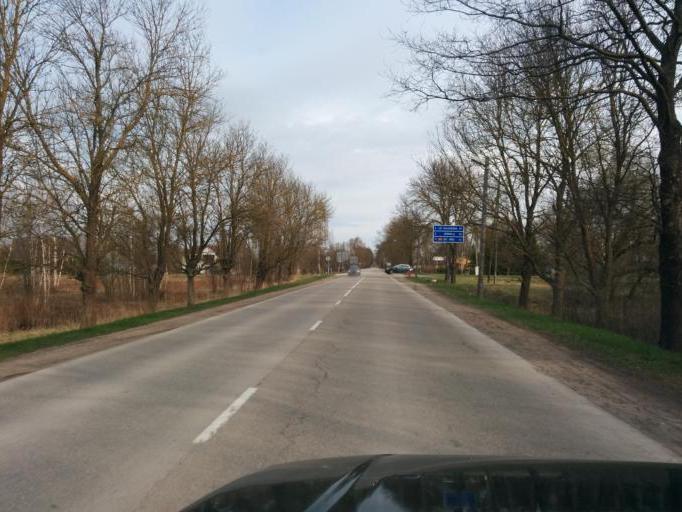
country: LV
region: Jelgava
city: Jelgava
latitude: 56.6684
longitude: 23.7318
